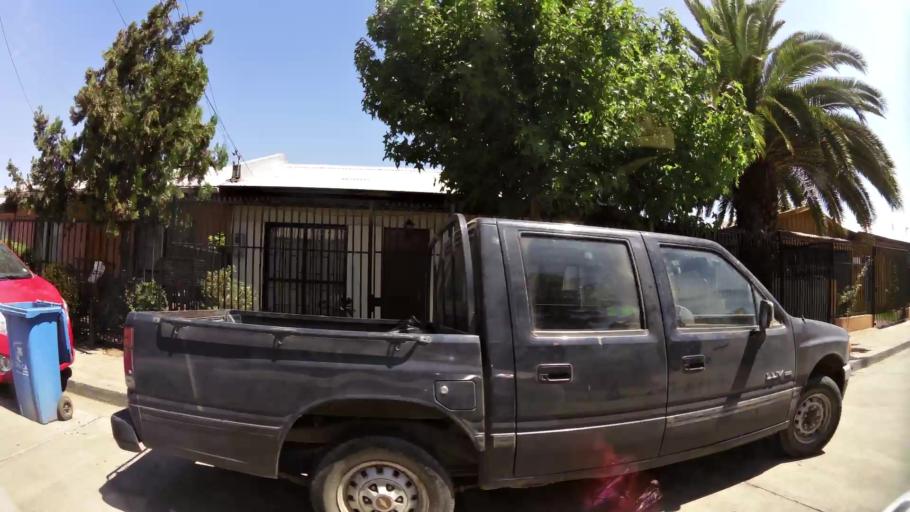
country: CL
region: Maule
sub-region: Provincia de Talca
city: Talca
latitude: -35.4266
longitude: -71.6284
